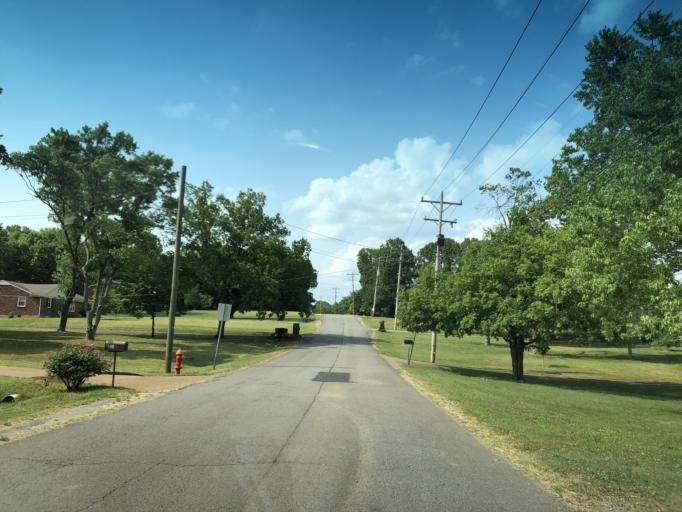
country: US
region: Tennessee
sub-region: Davidson County
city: Goodlettsville
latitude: 36.2589
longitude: -86.7214
